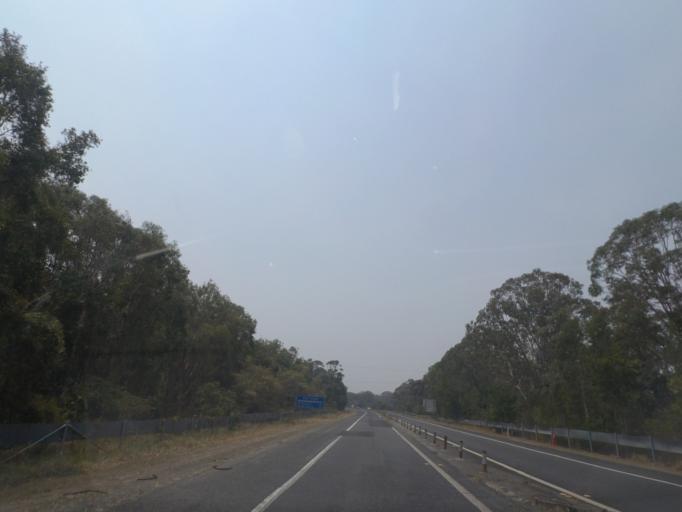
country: AU
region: New South Wales
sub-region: Ballina
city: Ballina
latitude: -28.9311
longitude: 153.4742
